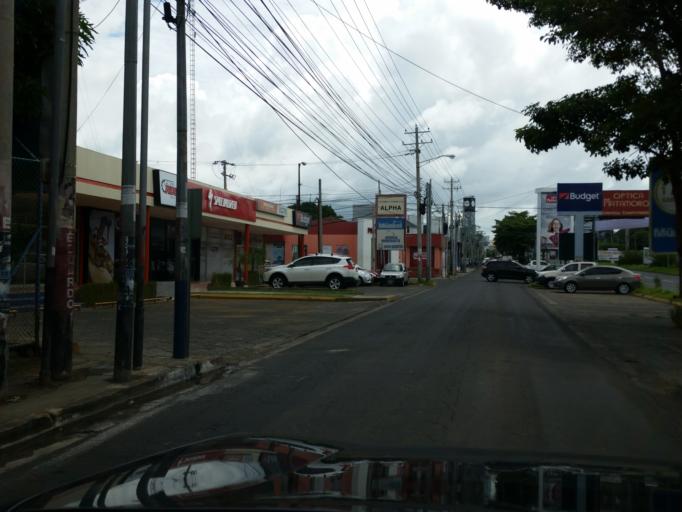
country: NI
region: Managua
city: Managua
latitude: 12.1181
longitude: -86.2594
